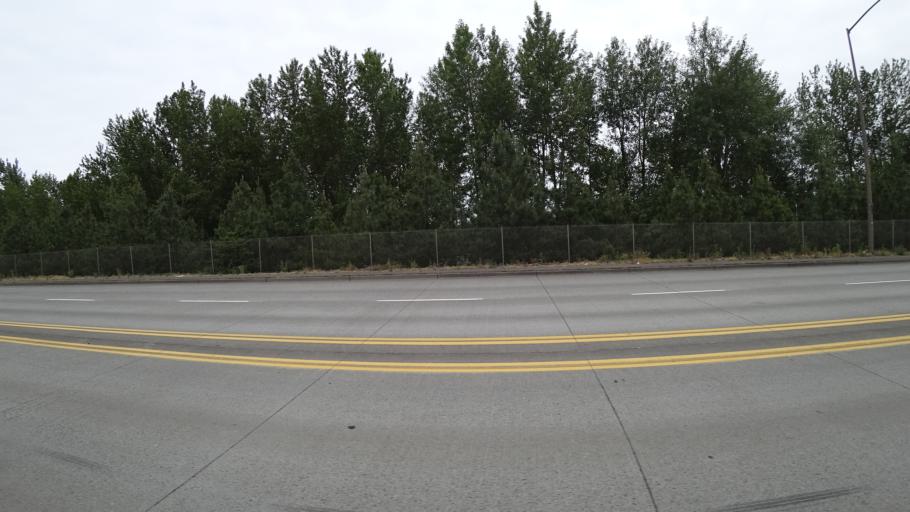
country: US
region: Washington
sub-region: Clark County
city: Vancouver
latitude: 45.6175
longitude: -122.7142
